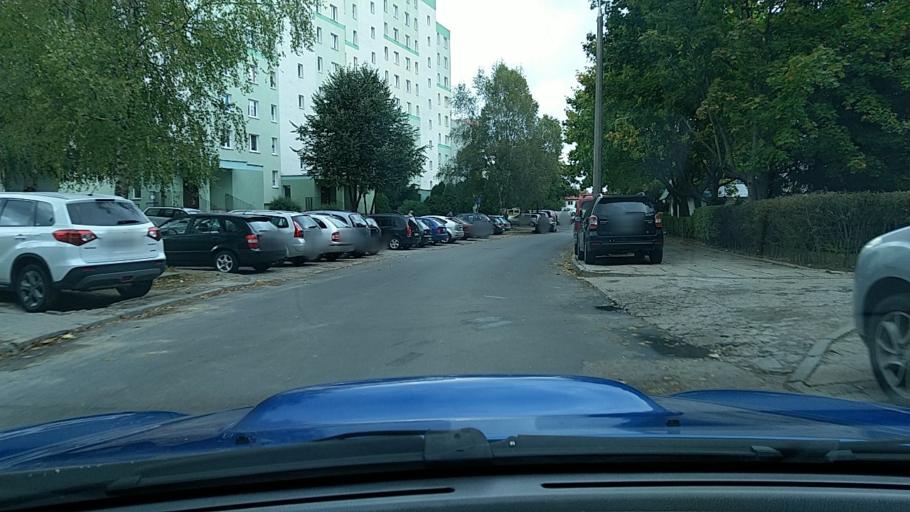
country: PL
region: Warmian-Masurian Voivodeship
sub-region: Olsztyn
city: Kortowo
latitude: 53.7416
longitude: 20.4815
